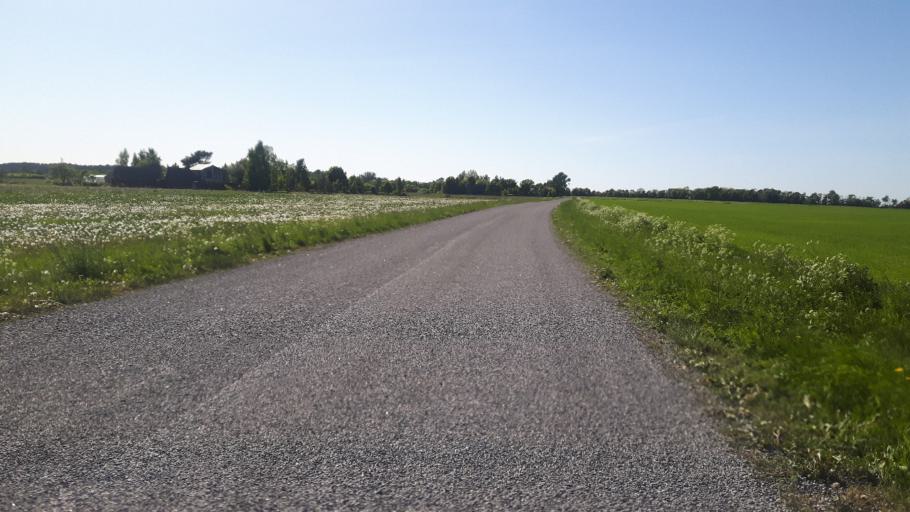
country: EE
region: Ida-Virumaa
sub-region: Kohtla-Jaerve linn
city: Kohtla-Jarve
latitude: 59.4350
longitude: 27.2041
